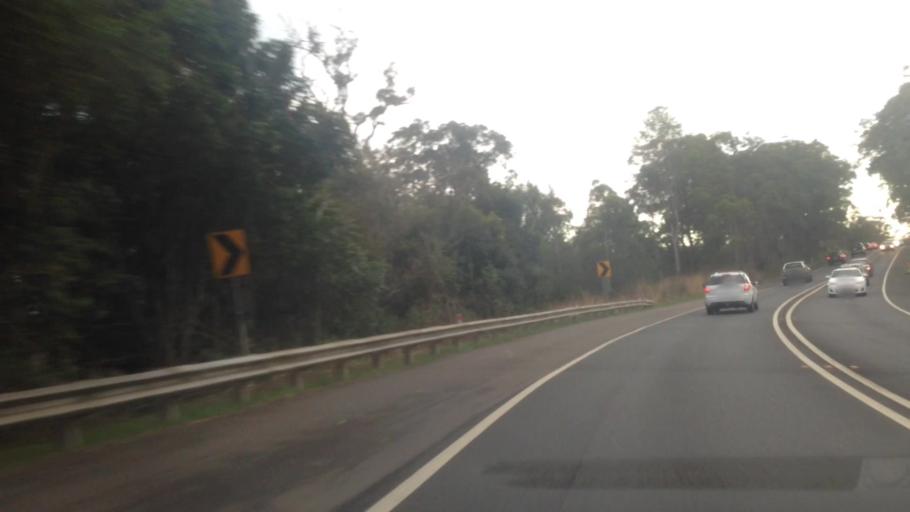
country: AU
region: New South Wales
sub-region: Wyong Shire
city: Tuggerawong
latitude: -33.2616
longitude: 151.4571
